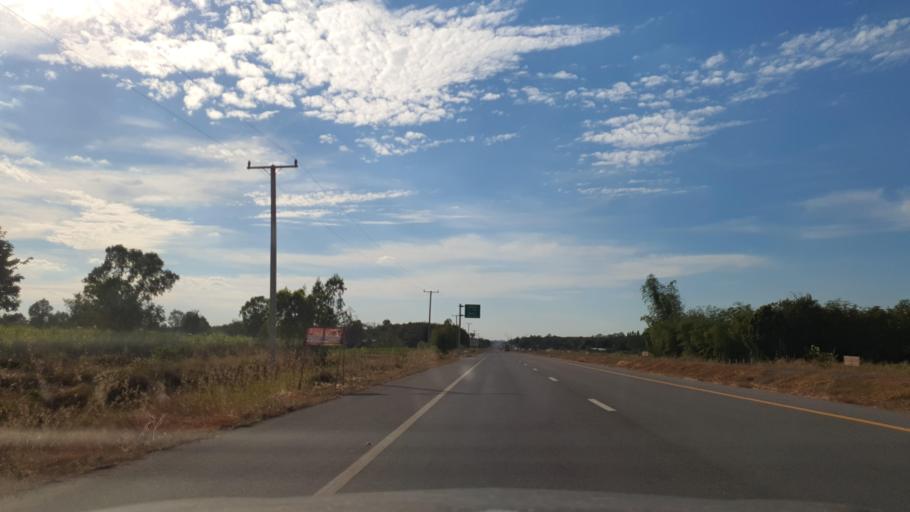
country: TH
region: Roi Et
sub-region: Amphoe Pho Chai
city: Pho Chai
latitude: 16.4143
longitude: 103.7968
